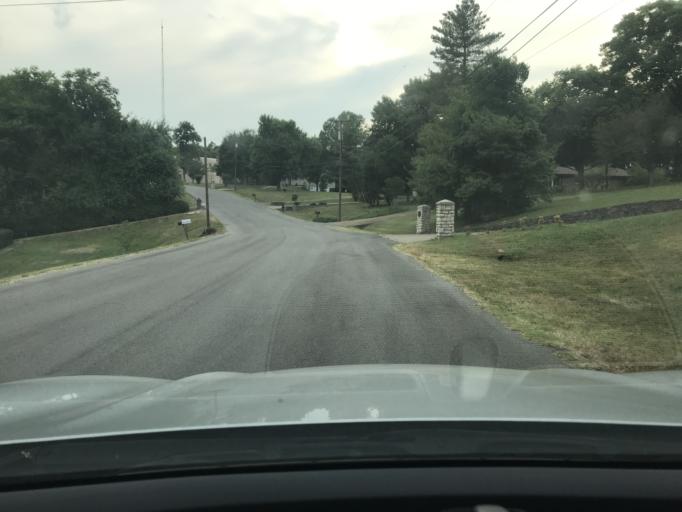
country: US
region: Tennessee
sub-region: Davidson County
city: Goodlettsville
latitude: 36.3114
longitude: -86.7194
